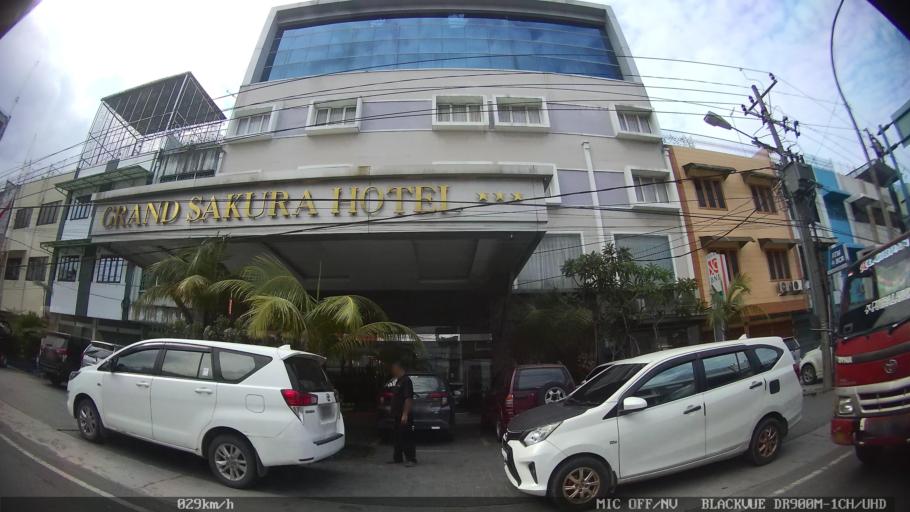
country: ID
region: North Sumatra
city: Medan
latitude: 3.5967
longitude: 98.6863
